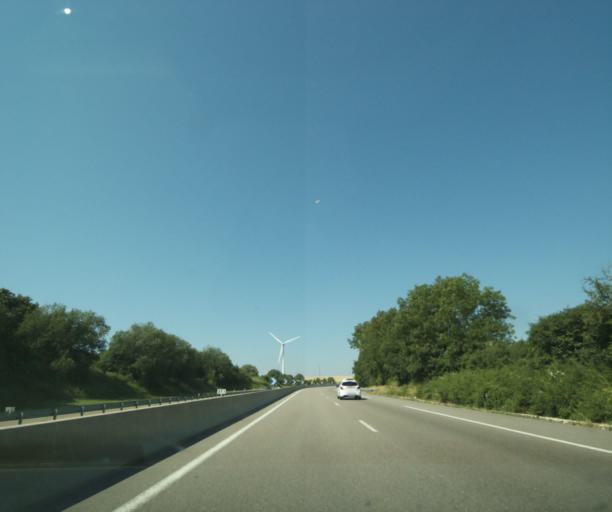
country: FR
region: Lorraine
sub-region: Departement de la Meuse
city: Ligny-en-Barrois
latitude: 48.7038
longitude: 5.4441
